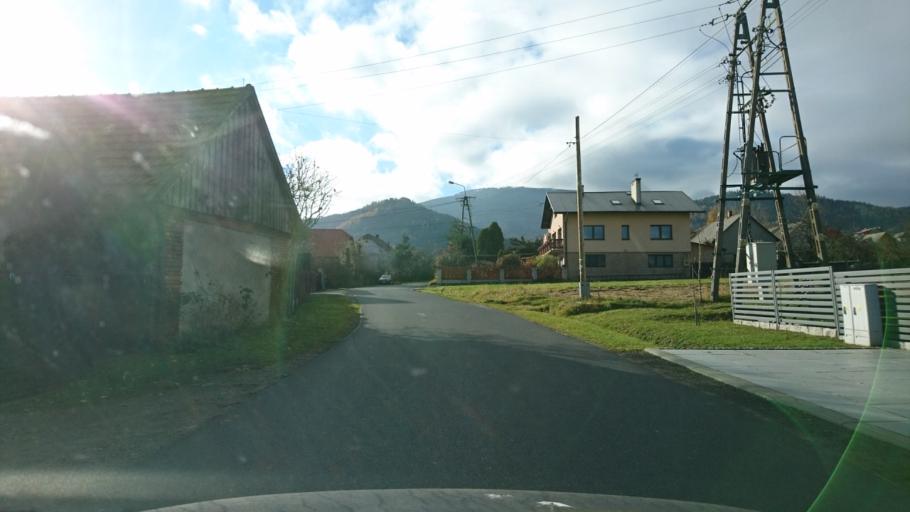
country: PL
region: Silesian Voivodeship
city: Godziszka
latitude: 49.7015
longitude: 19.0807
